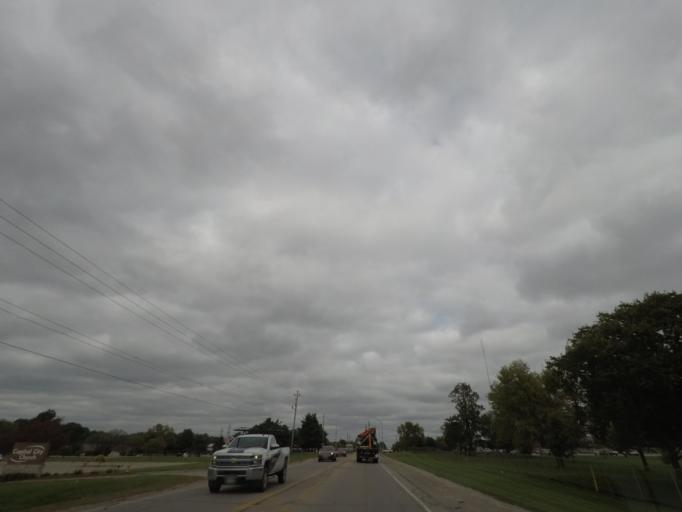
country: US
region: Iowa
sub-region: Polk County
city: Saylorville
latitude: 41.6680
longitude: -93.6007
